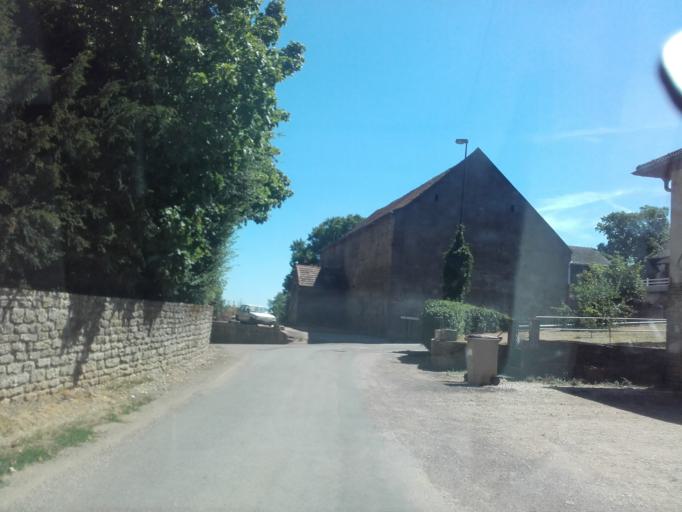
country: FR
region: Bourgogne
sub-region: Departement de Saone-et-Loire
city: Buxy
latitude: 46.7518
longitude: 4.6771
